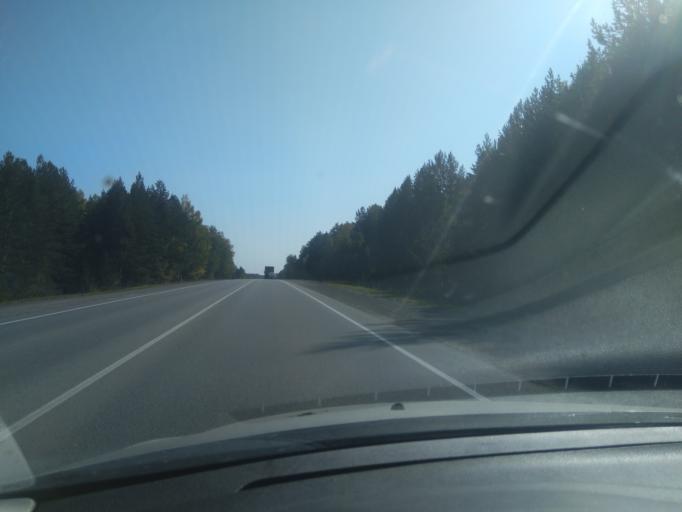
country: RU
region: Sverdlovsk
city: Verkhneye Dubrovo
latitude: 56.7038
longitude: 61.0765
